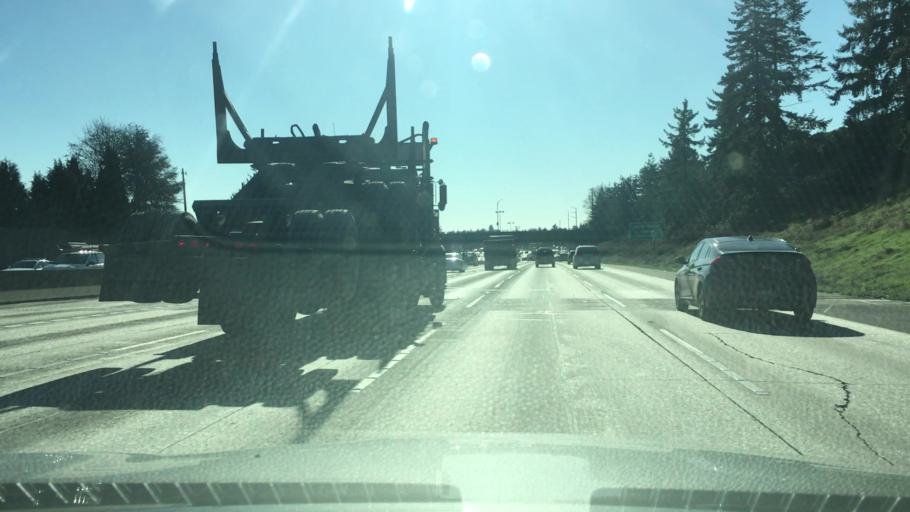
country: US
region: Washington
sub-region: King County
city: Shoreline
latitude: 47.7148
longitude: -122.3253
